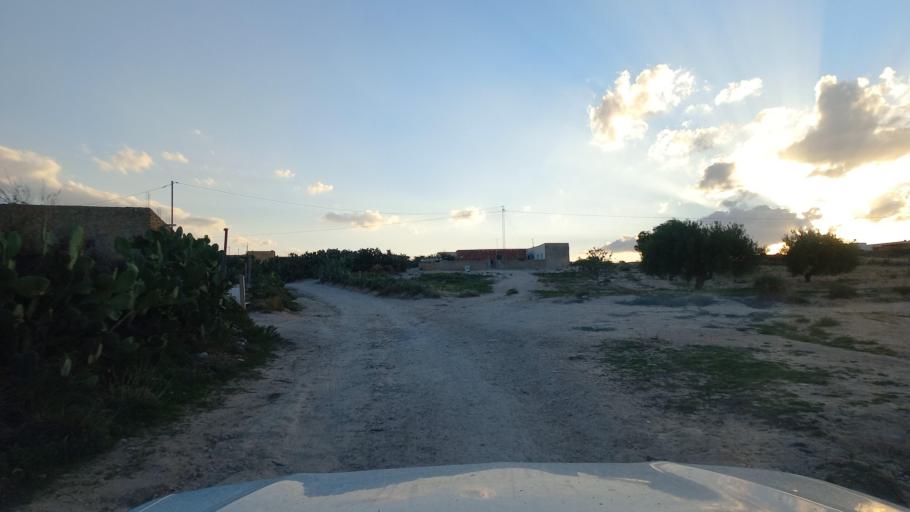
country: TN
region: Al Qasrayn
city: Sbiba
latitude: 35.3721
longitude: 9.0662
